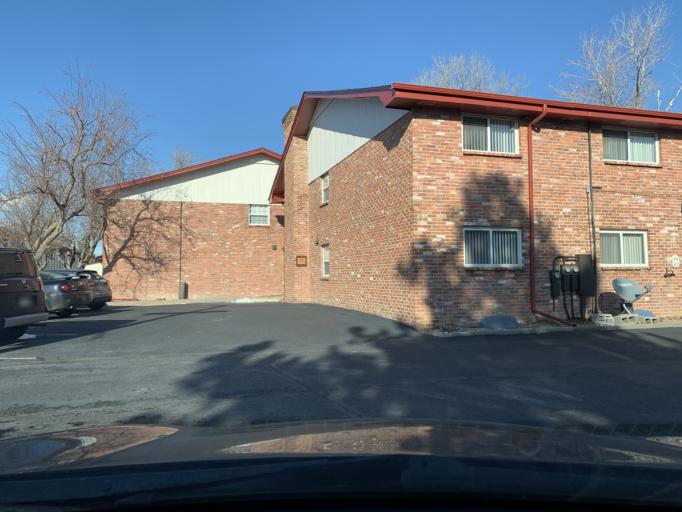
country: US
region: Colorado
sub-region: Jefferson County
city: Applewood
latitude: 39.7465
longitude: -105.1253
